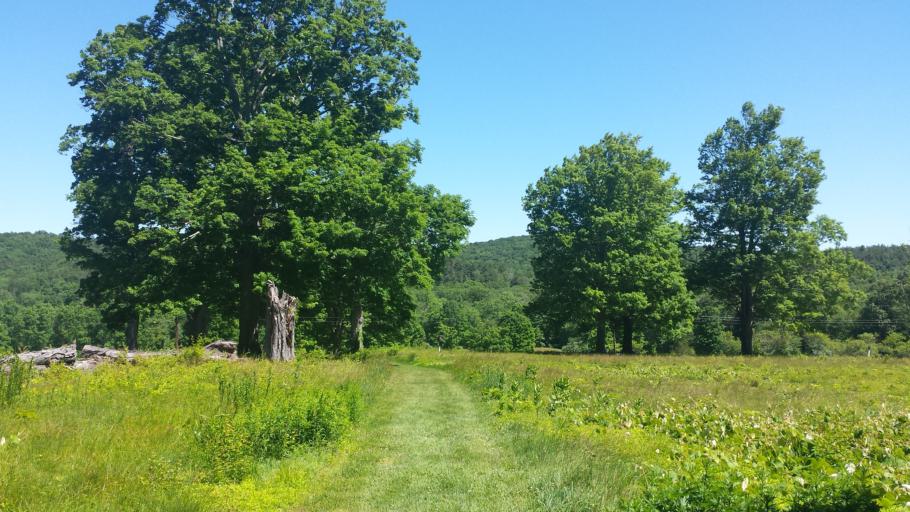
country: US
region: New York
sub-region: Westchester County
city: Pound Ridge
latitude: 41.2571
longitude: -73.5958
